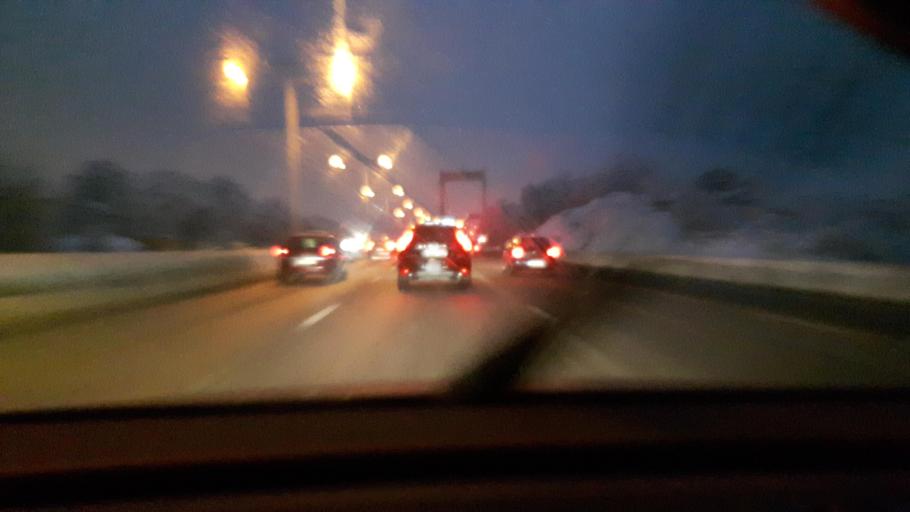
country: SE
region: Vaestra Goetaland
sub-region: Goteborg
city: Majorna
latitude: 57.6972
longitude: 11.8972
